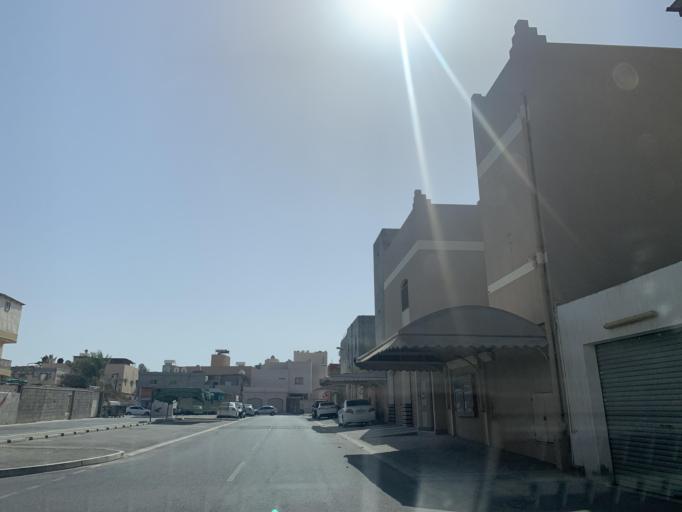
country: BH
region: Manama
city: Jidd Hafs
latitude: 26.2323
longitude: 50.4832
